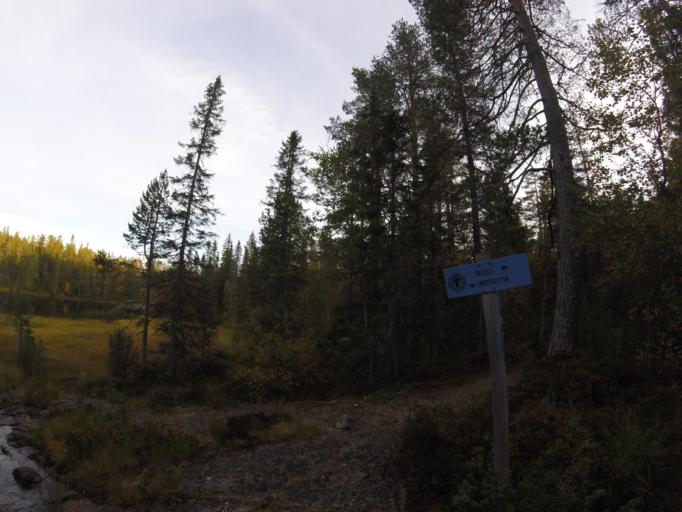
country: NO
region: Buskerud
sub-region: Kongsberg
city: Kongsberg
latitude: 59.6787
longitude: 9.4623
